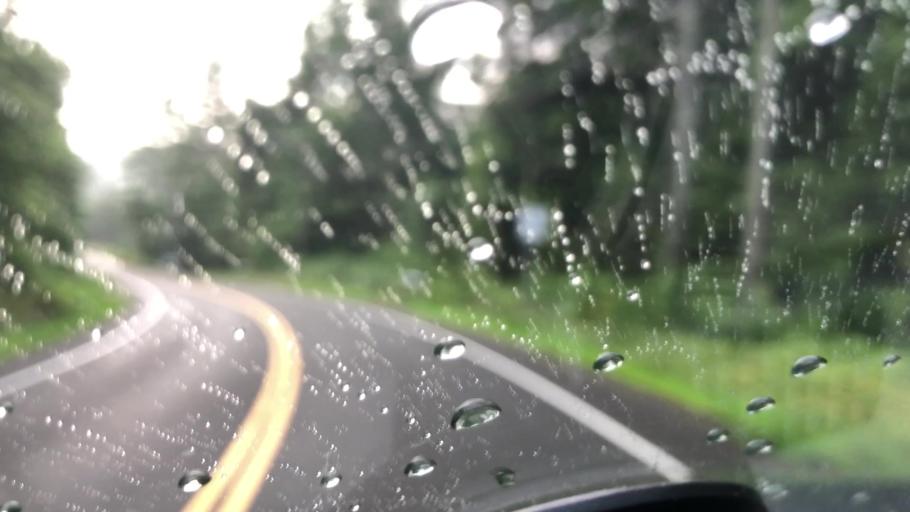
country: US
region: Massachusetts
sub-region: Hampshire County
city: Westhampton
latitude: 42.2824
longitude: -72.8621
